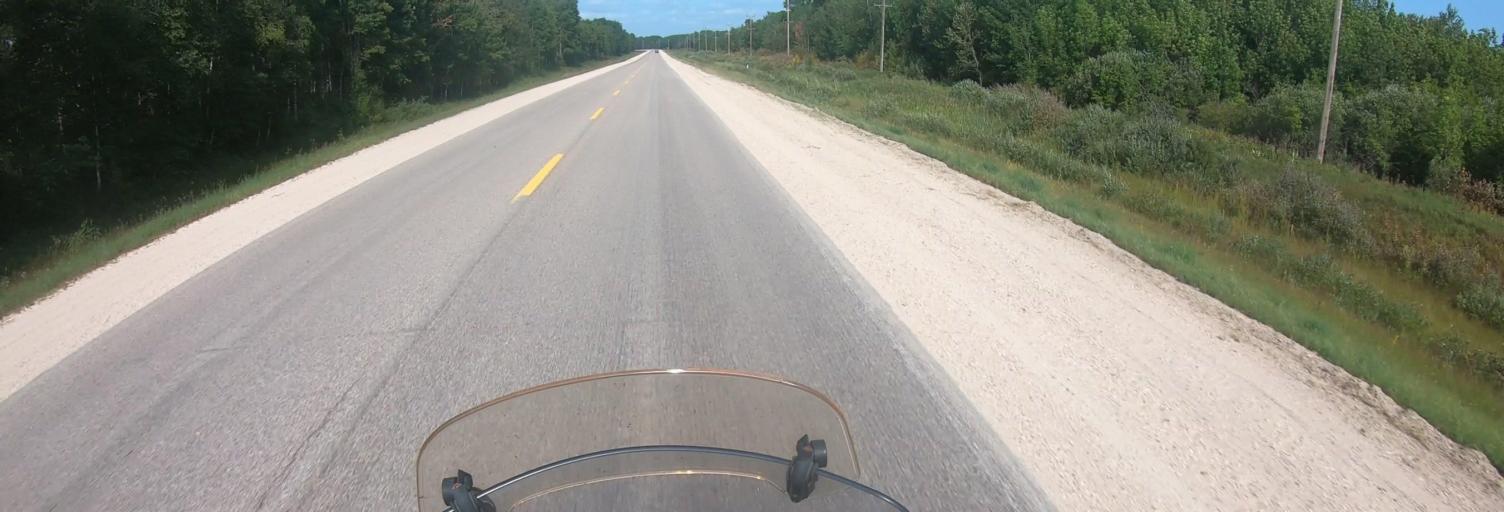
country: CA
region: Manitoba
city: La Broquerie
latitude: 49.1685
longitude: -96.1522
